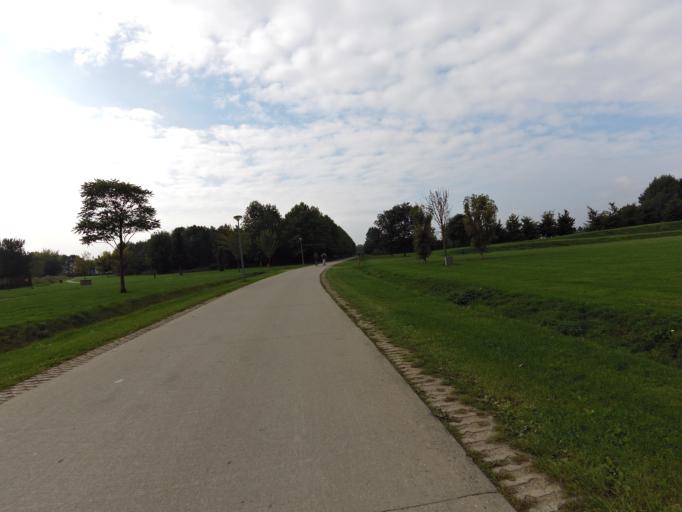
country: NL
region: Gelderland
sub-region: Gemeente Westervoort
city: Westervoort
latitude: 51.9479
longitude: 5.9920
